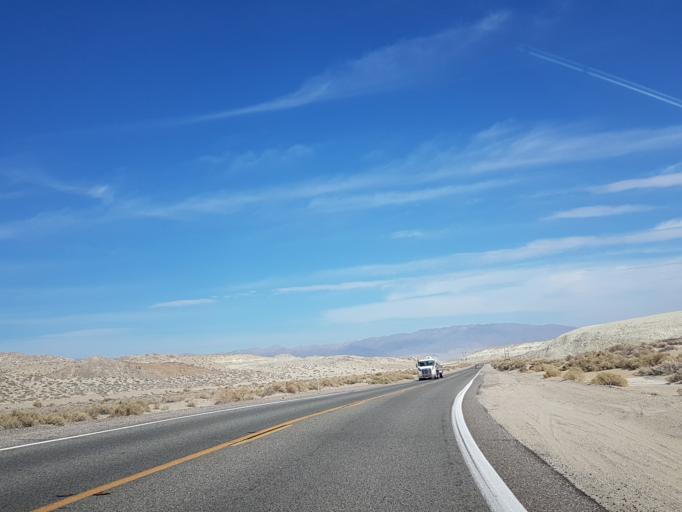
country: US
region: California
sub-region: San Bernardino County
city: Searles Valley
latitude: 35.6684
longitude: -117.4246
